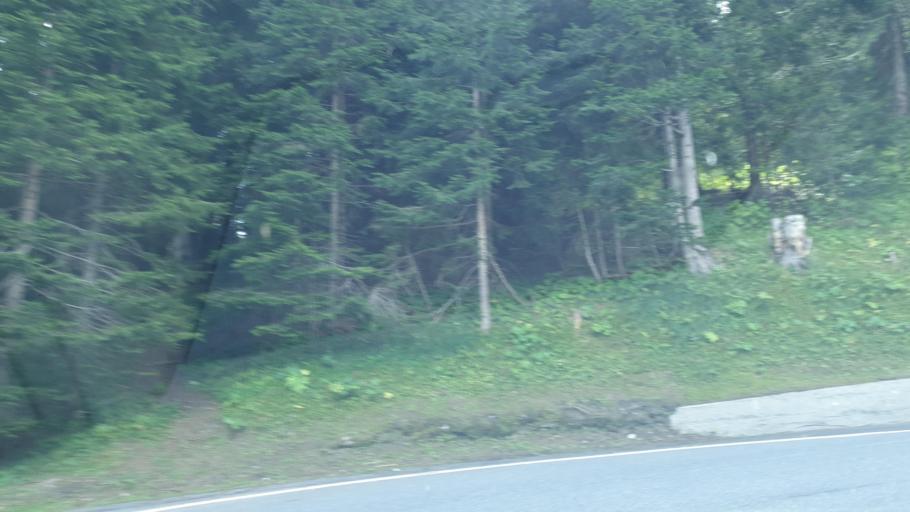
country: CH
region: Grisons
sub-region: Hinterrhein District
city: Hinterrhein
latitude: 46.5458
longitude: 9.3237
